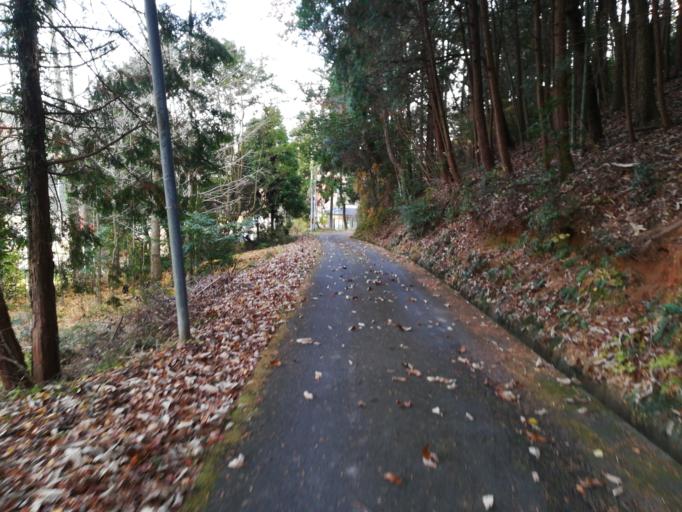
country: JP
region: Kyoto
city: Kameoka
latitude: 34.9733
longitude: 135.5021
